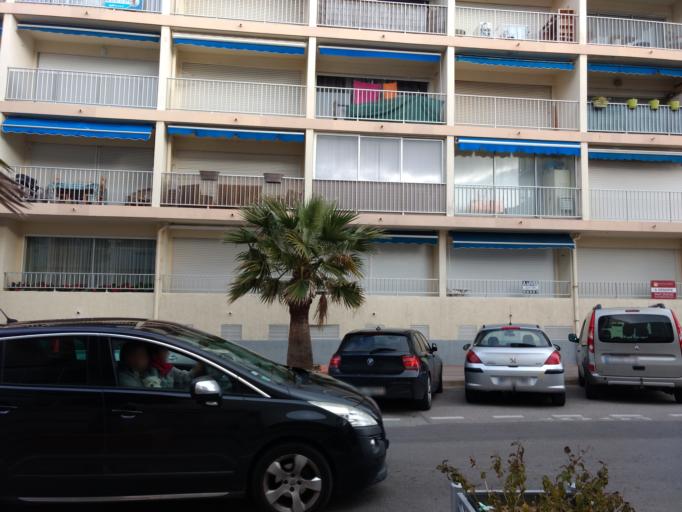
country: FR
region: Languedoc-Roussillon
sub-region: Departement de l'Herault
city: Palavas-les-Flots
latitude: 43.5260
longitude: 3.9276
